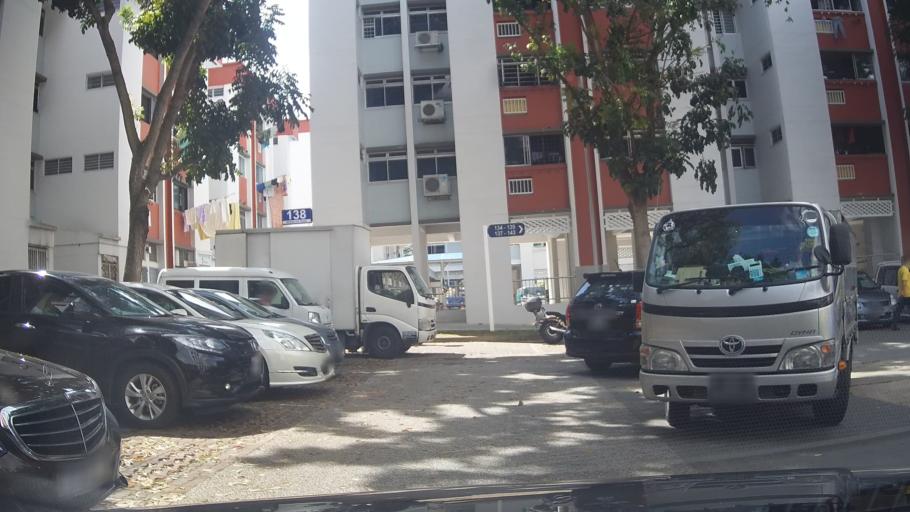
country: MY
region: Johor
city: Johor Bahru
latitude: 1.4385
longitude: 103.7776
